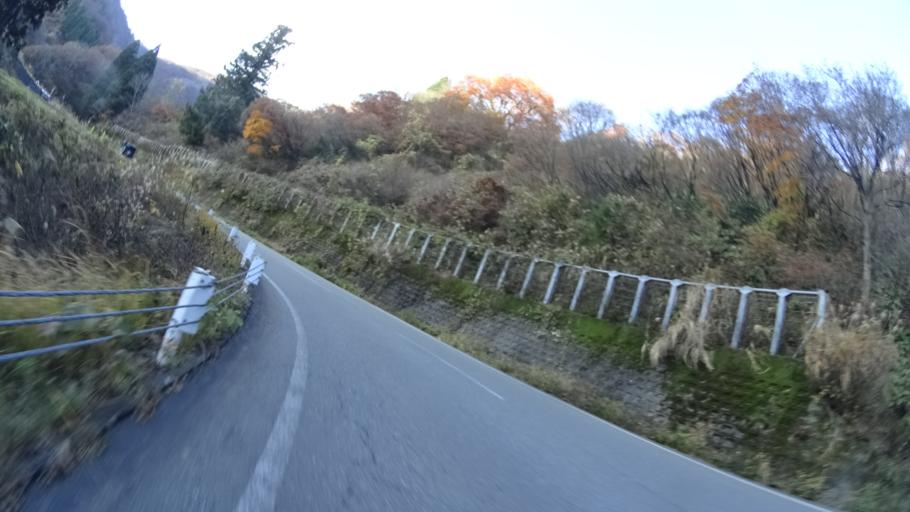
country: JP
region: Niigata
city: Shiozawa
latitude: 36.9865
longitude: 138.7839
